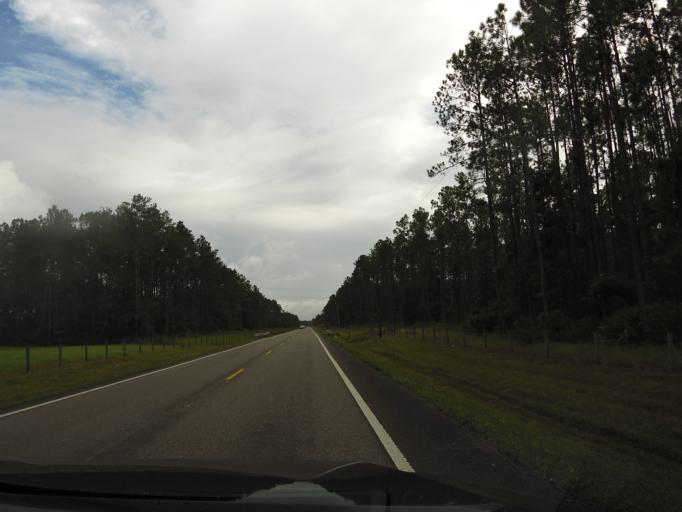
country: US
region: Florida
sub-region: Duval County
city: Baldwin
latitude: 30.3558
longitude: -81.9147
